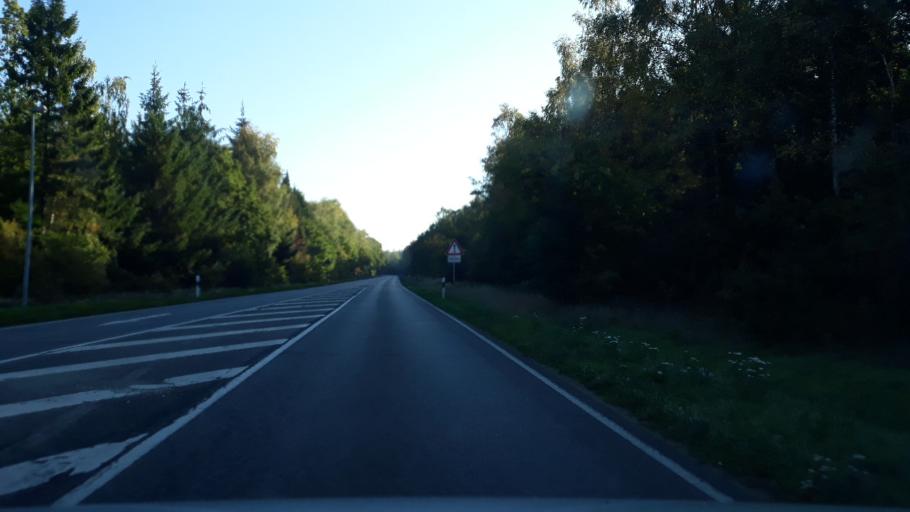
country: DE
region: Schleswig-Holstein
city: Kropp
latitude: 54.4035
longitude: 9.5125
